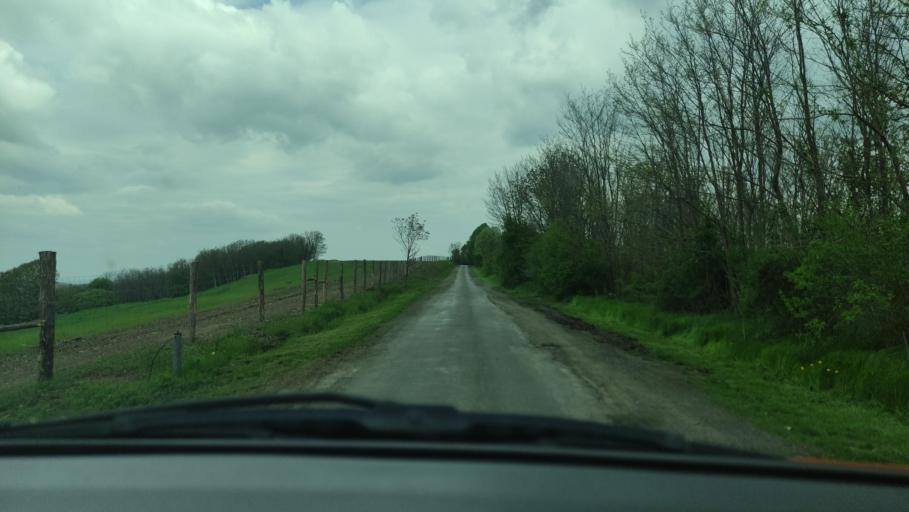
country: HU
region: Somogy
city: Taszar
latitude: 46.2947
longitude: 17.9649
